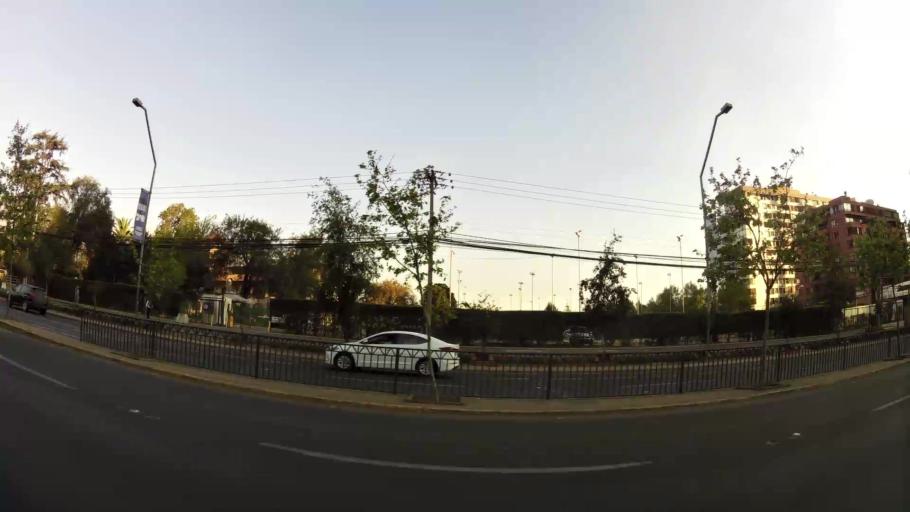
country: CL
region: Santiago Metropolitan
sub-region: Provincia de Santiago
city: Villa Presidente Frei, Nunoa, Santiago, Chile
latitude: -33.4076
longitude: -70.5628
